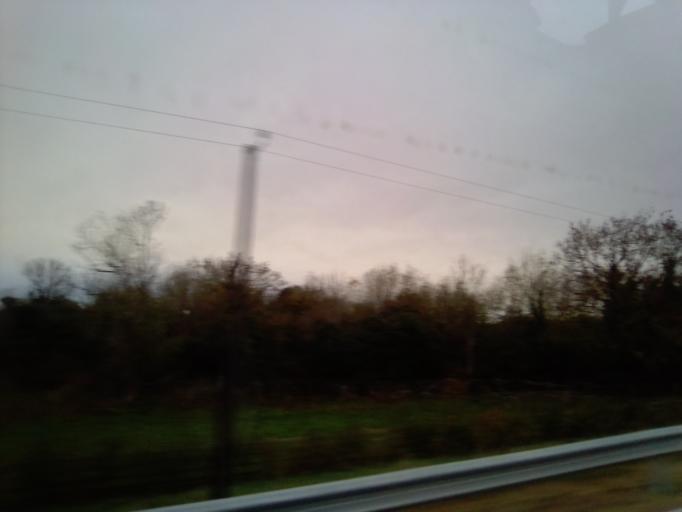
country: IE
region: Connaught
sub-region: County Galway
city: Oranmore
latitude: 53.2130
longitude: -8.8299
